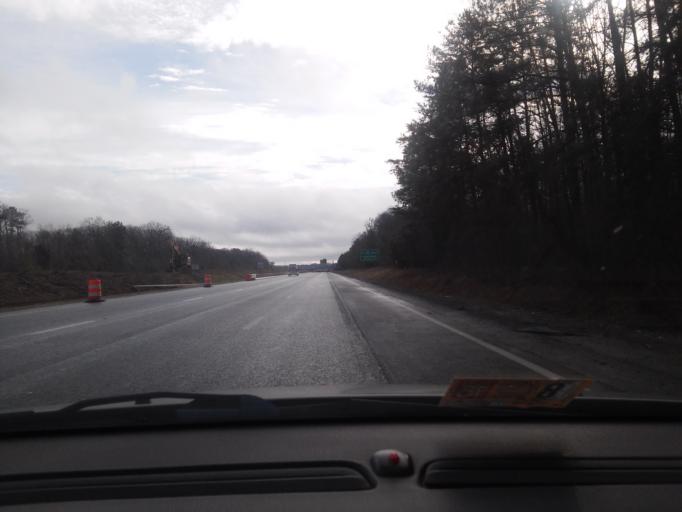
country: US
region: Virginia
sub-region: Henrico County
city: Wyndham
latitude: 37.6802
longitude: -77.6639
